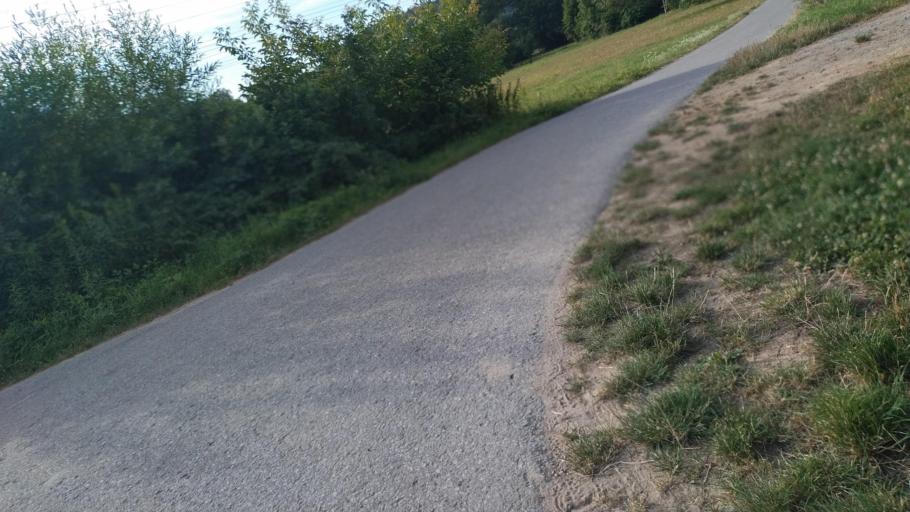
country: DE
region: Baden-Wuerttemberg
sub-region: Karlsruhe Region
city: Karlsruhe
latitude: 48.9785
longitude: 8.4421
